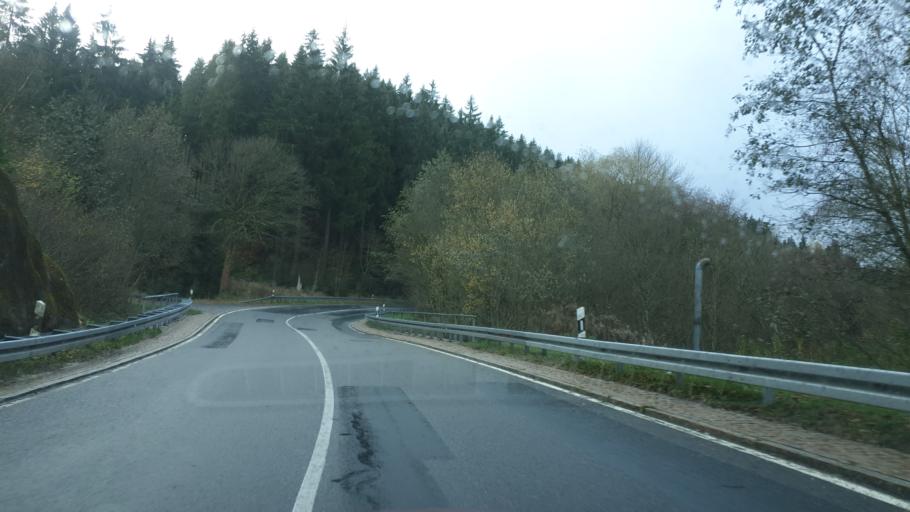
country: DE
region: Saxony
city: Schoenheide
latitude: 50.4836
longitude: 12.5422
